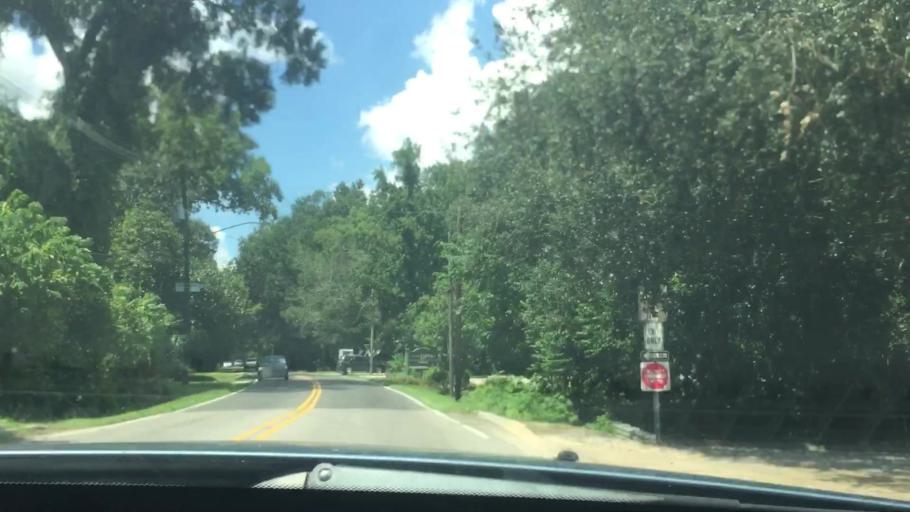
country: US
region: Louisiana
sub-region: East Baton Rouge Parish
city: Gardere
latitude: 30.3692
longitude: -91.1231
